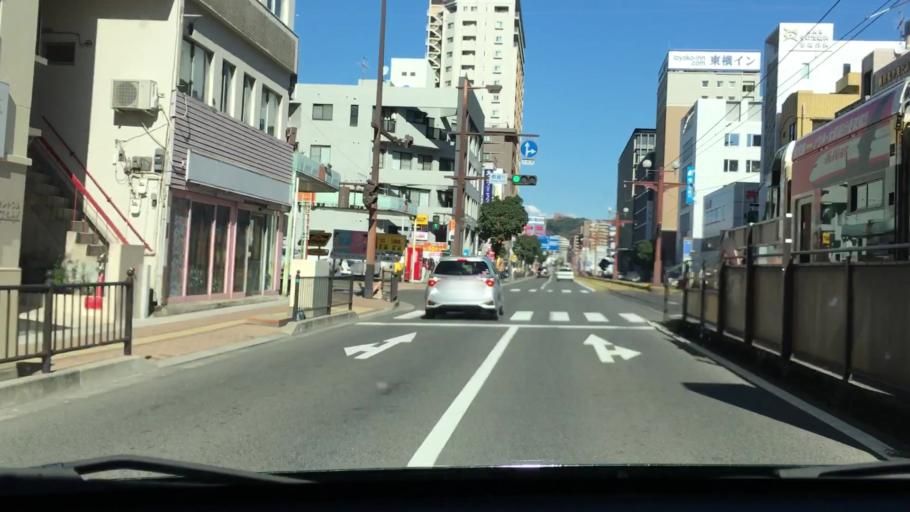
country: JP
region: Kagoshima
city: Kagoshima-shi
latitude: 31.5803
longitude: 130.5429
